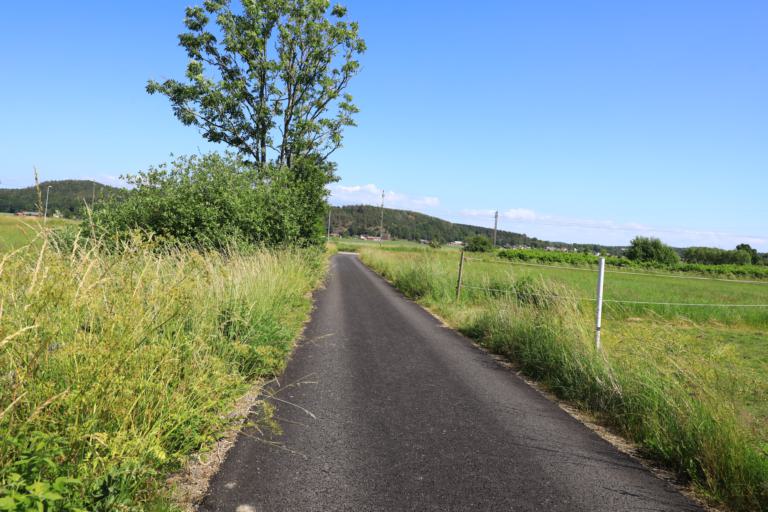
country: SE
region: Halland
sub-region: Varbergs Kommun
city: Varberg
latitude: 57.1757
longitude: 12.3006
